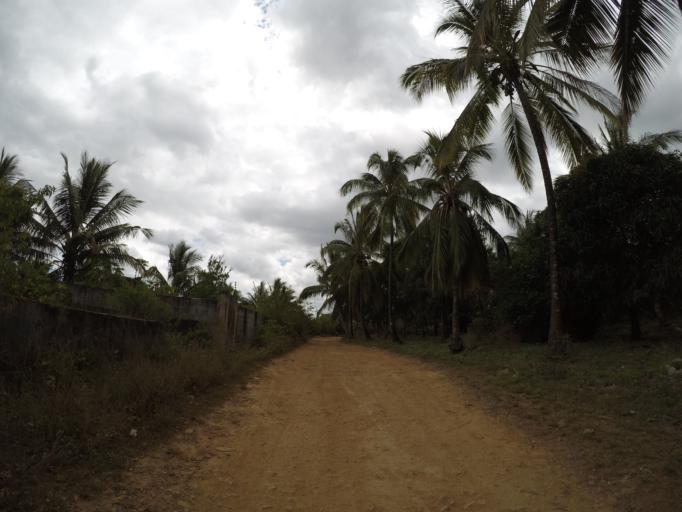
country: TZ
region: Zanzibar Central/South
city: Koani
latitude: -6.1934
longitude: 39.3069
